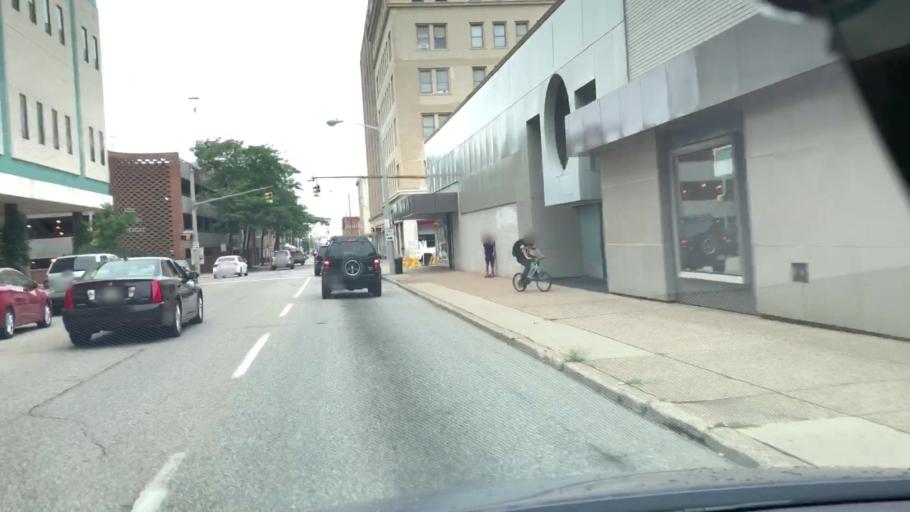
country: US
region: Pennsylvania
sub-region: Erie County
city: Erie
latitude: 42.1266
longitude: -80.0850
